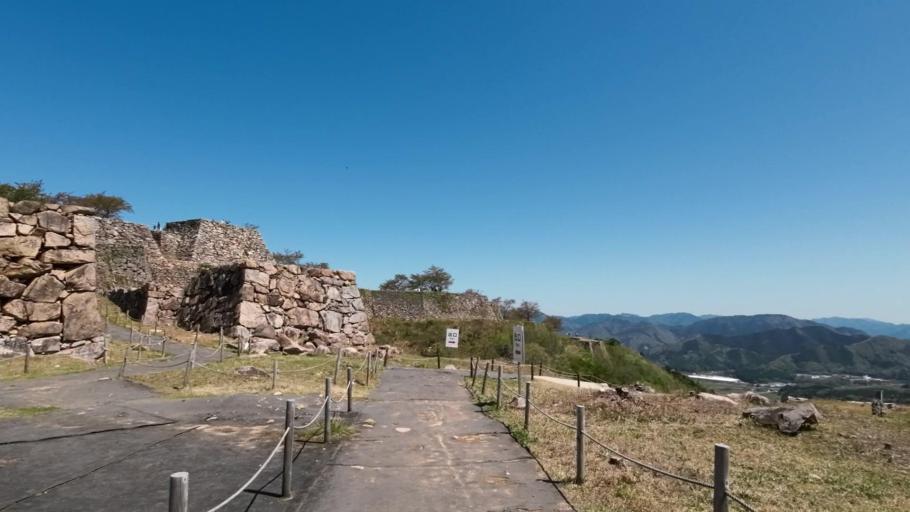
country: JP
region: Hyogo
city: Toyooka
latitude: 35.2996
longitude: 134.8292
